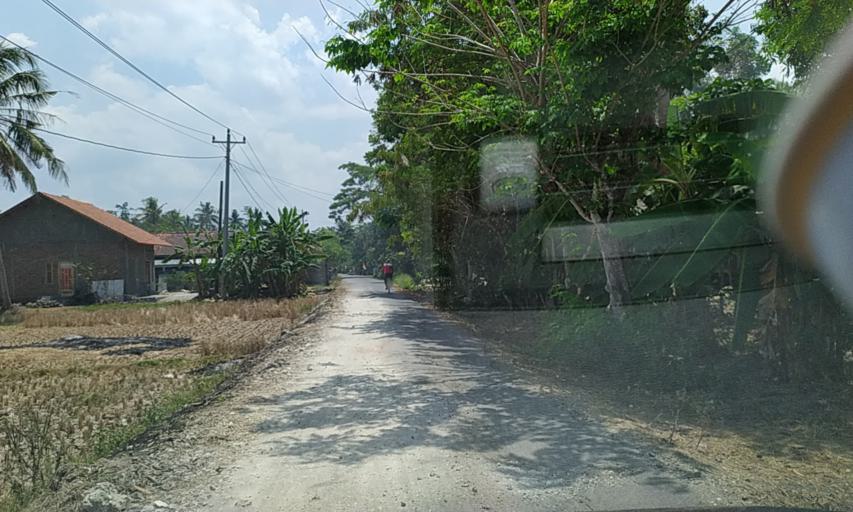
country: ID
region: Central Java
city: Pondokwungu
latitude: -7.5606
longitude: 108.8022
